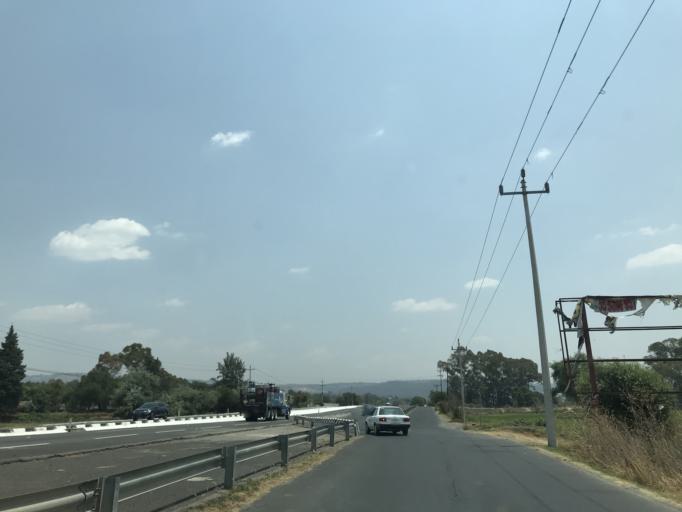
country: MX
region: Tlaxcala
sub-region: Ixtacuixtla de Mariano Matamoros
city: Villa Mariano Matamoros
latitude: 19.3211
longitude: -98.3725
